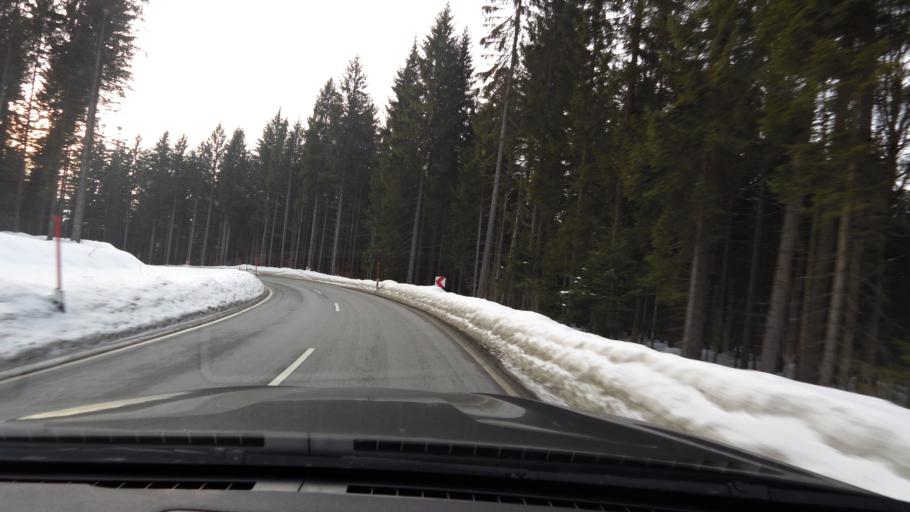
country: DE
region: Bavaria
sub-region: Lower Bavaria
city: Philippsreut
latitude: 48.8665
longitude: 13.7235
